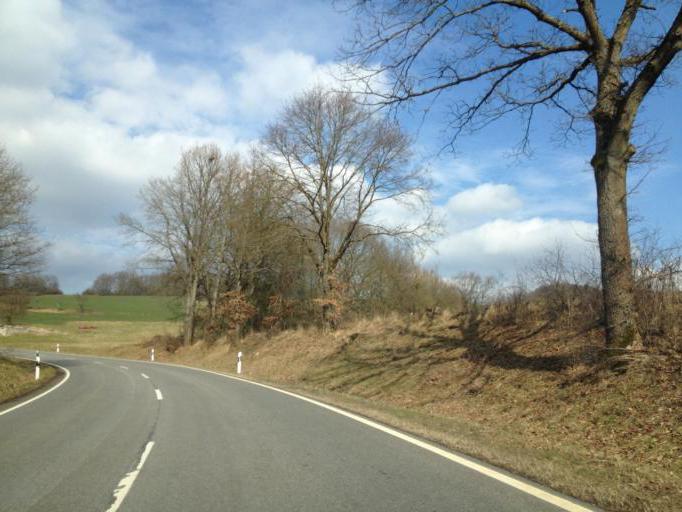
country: DE
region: Rheinland-Pfalz
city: Selchenbach
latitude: 49.4993
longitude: 7.3013
